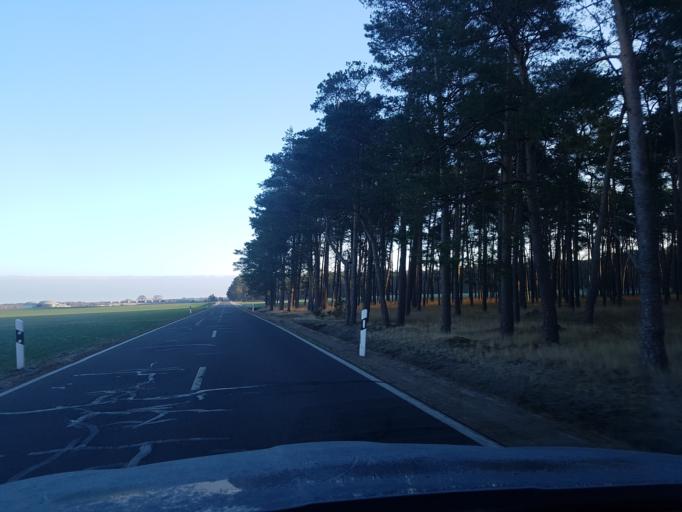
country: DE
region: Brandenburg
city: Schlieben
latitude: 51.6860
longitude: 13.3215
